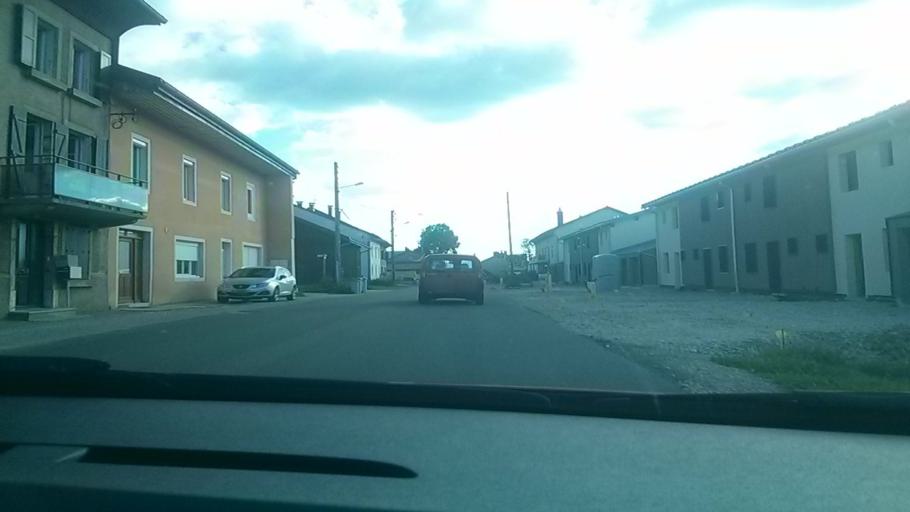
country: CH
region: Vaud
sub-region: Nyon District
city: Saint-Cergue
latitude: 46.5350
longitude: 6.1412
